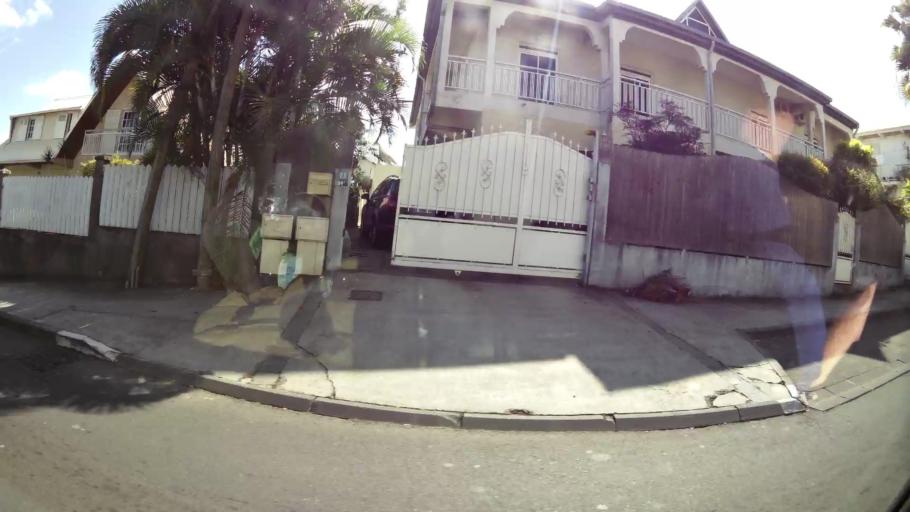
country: RE
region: Reunion
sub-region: Reunion
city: Le Tampon
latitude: -21.2808
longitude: 55.5121
